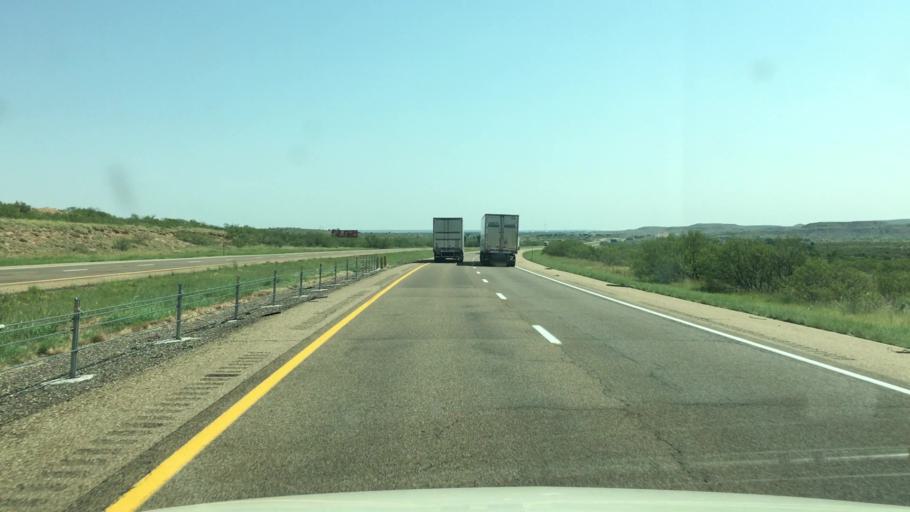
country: US
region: New Mexico
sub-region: Quay County
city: Tucumcari
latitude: 35.1395
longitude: -103.8265
